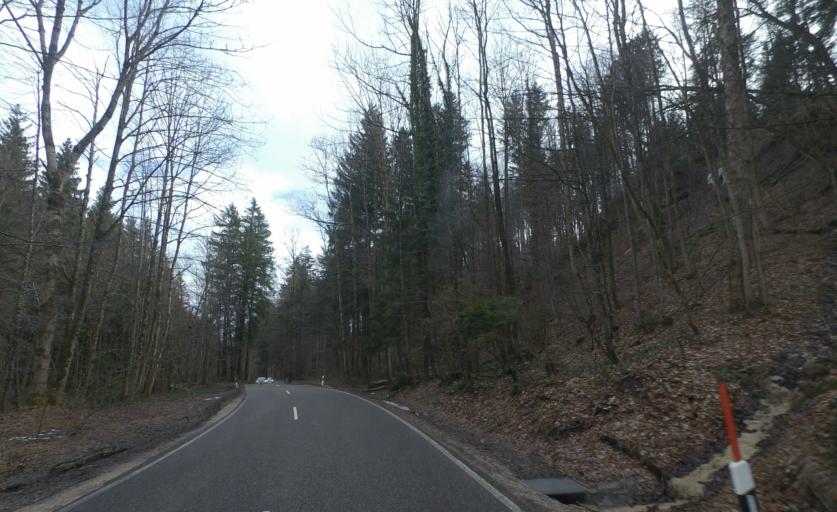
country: DE
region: Bavaria
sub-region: Upper Bavaria
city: Inzell
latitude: 47.8310
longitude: 12.7548
